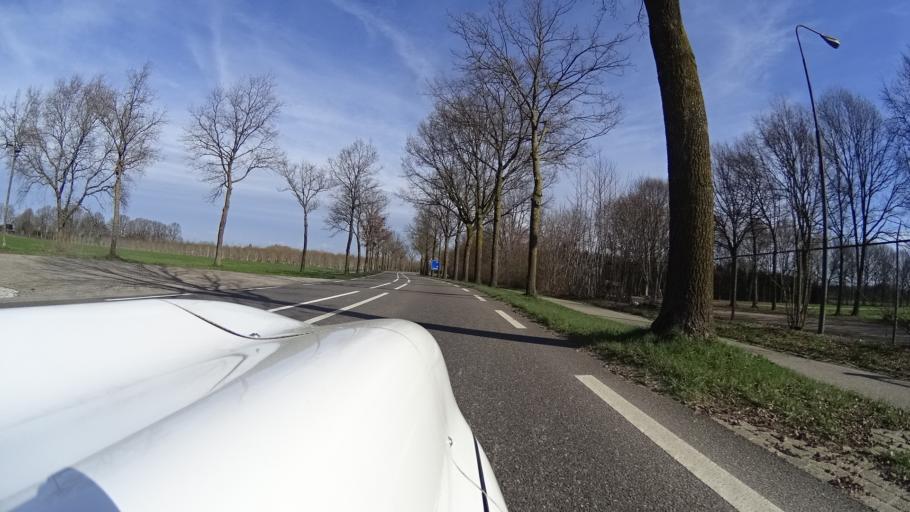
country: NL
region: North Brabant
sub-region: Gemeente Cuijk
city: Cuijk
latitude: 51.7114
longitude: 5.8596
